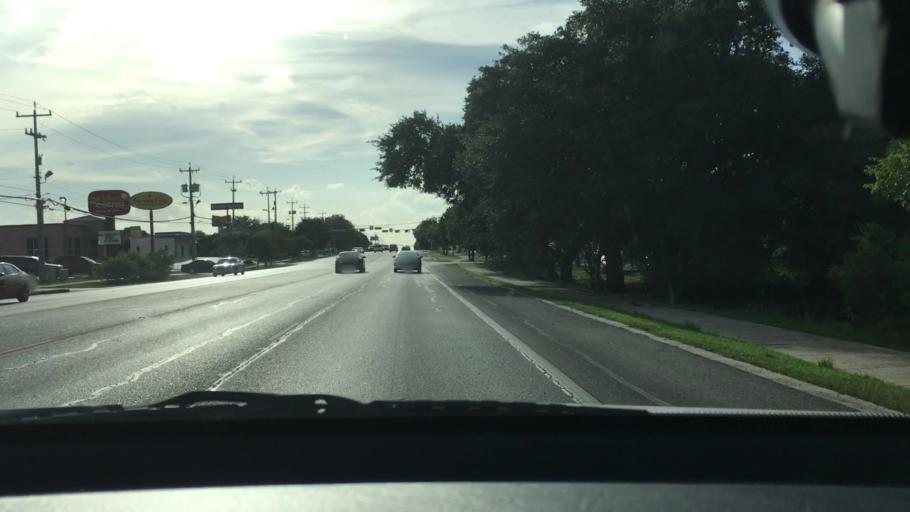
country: US
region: Texas
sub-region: Bexar County
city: Universal City
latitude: 29.5551
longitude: -98.3138
